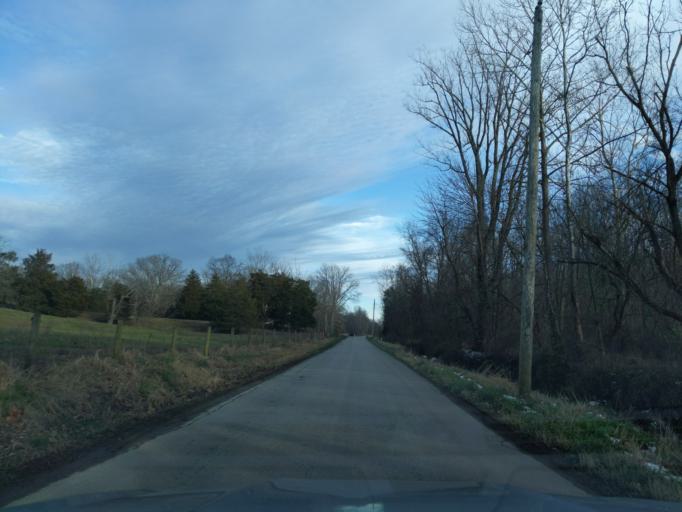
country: US
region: Indiana
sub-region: Decatur County
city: Westport
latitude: 39.2196
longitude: -85.5128
